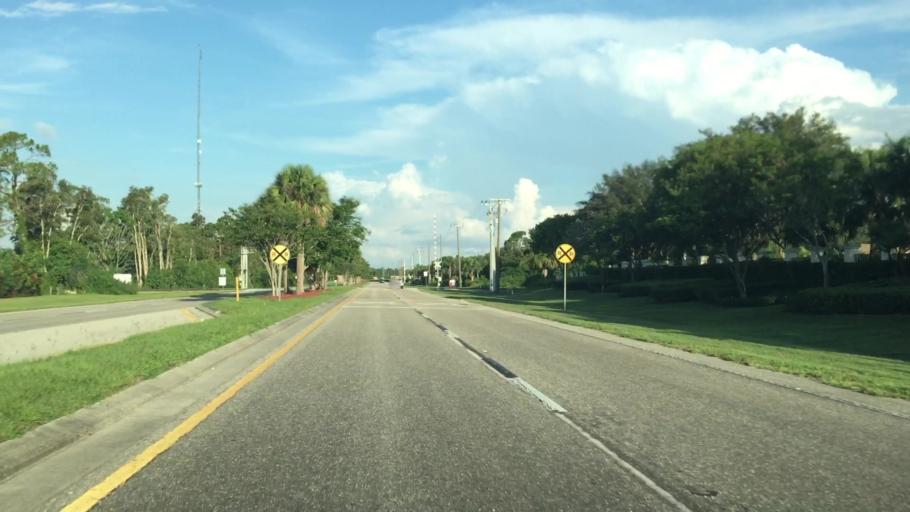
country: US
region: Florida
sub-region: Lee County
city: Estero
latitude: 26.4493
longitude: -81.8091
